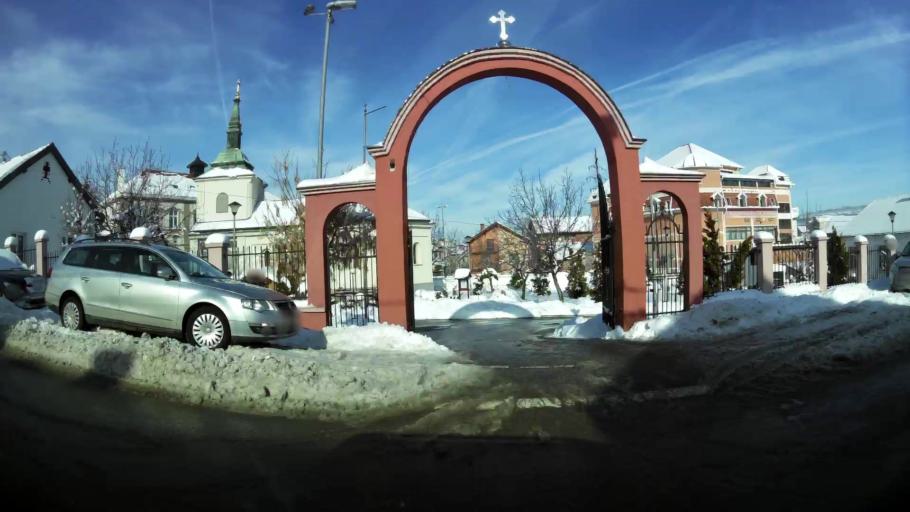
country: RS
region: Central Serbia
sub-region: Belgrade
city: Zvezdara
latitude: 44.7943
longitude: 20.5271
